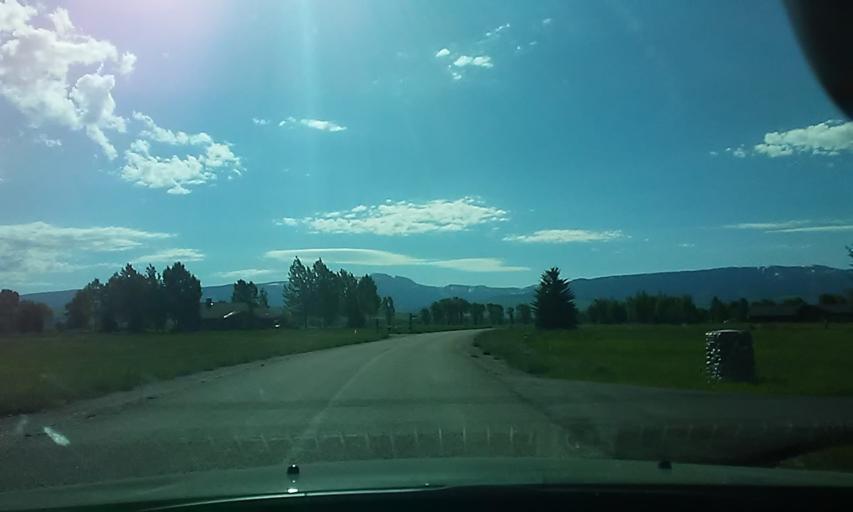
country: US
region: Wyoming
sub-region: Teton County
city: Jackson
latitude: 43.5774
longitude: -110.7482
